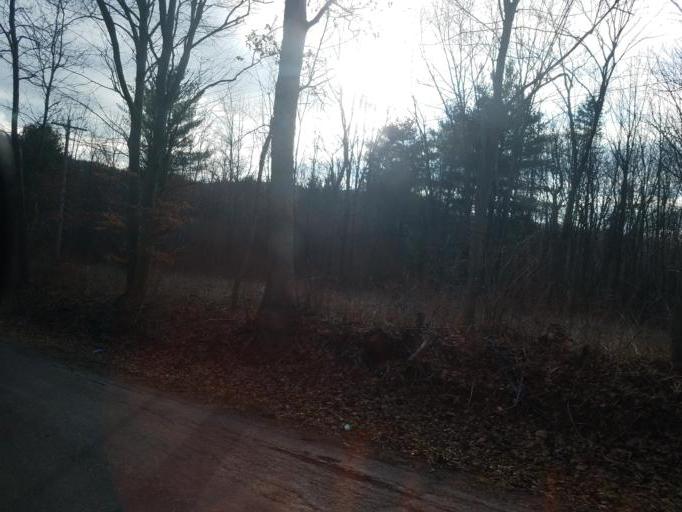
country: US
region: Ohio
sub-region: Sandusky County
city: Bellville
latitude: 40.6041
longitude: -82.3771
